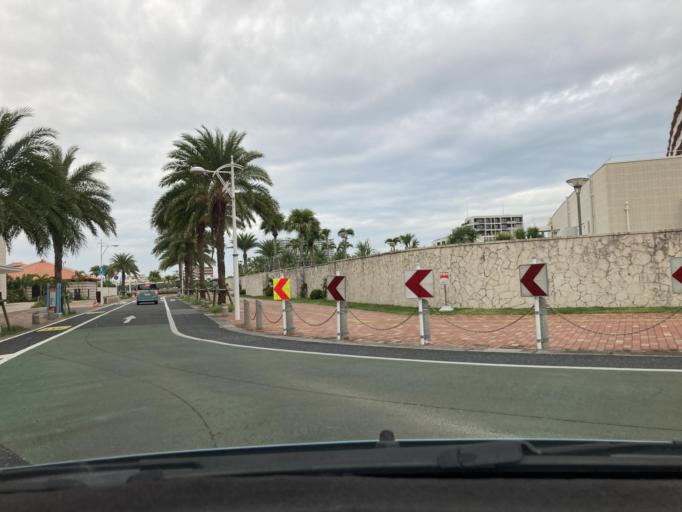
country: JP
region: Okinawa
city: Chatan
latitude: 26.3174
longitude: 127.7542
